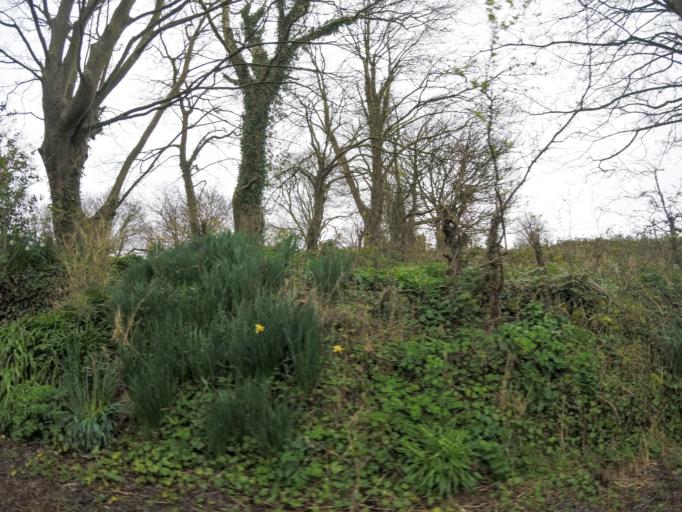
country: IE
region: Munster
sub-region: Waterford
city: Dunmore East
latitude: 52.2695
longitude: -6.9919
